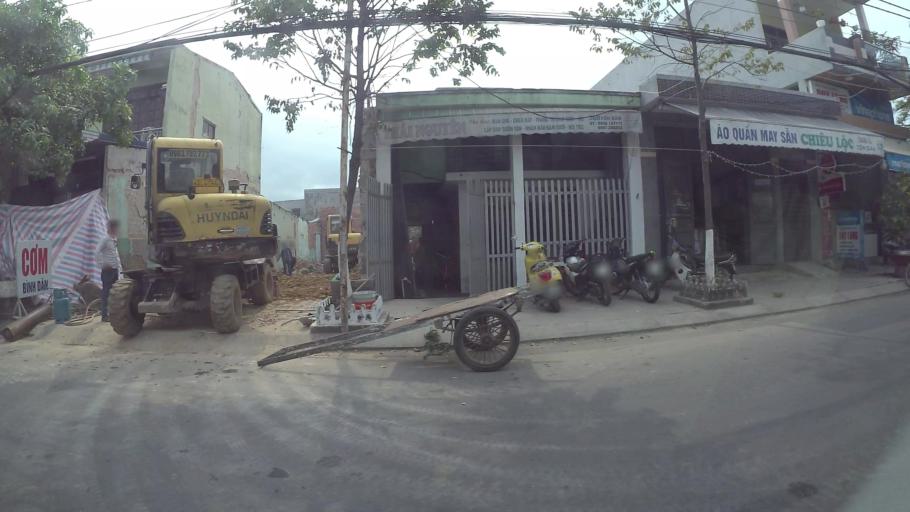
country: VN
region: Da Nang
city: Thanh Khe
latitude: 16.0471
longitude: 108.1817
